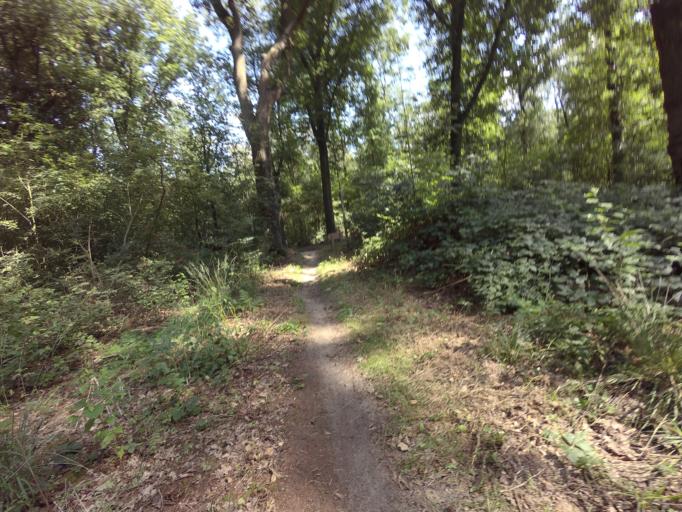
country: NL
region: Overijssel
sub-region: Gemeente Deventer
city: Schalkhaar
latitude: 52.2855
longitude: 6.2440
